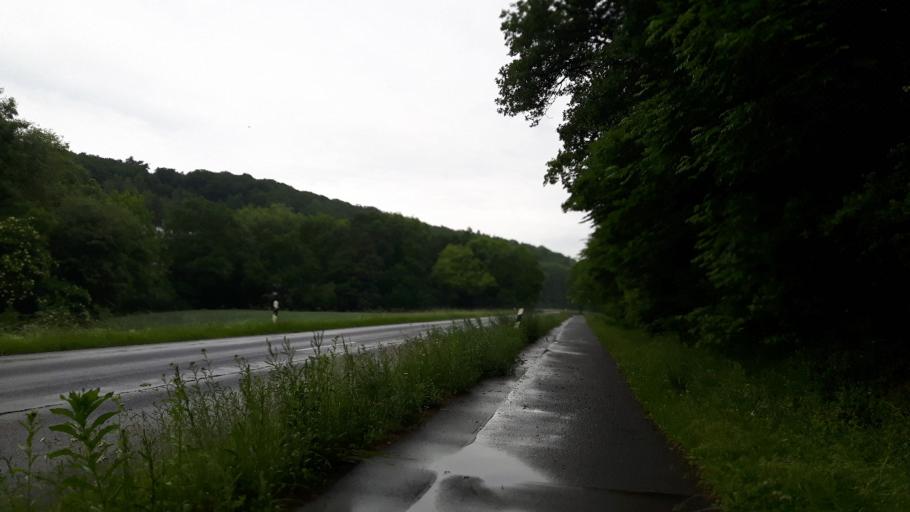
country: DE
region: Bavaria
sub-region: Regierungsbezirk Unterfranken
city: Schweinfurt
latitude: 50.0685
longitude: 10.2362
